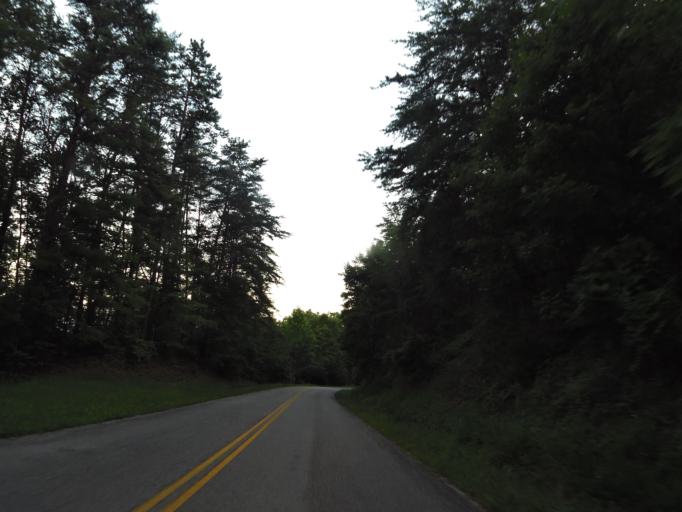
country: US
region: Tennessee
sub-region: Blount County
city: Maryville
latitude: 35.5936
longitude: -83.9906
